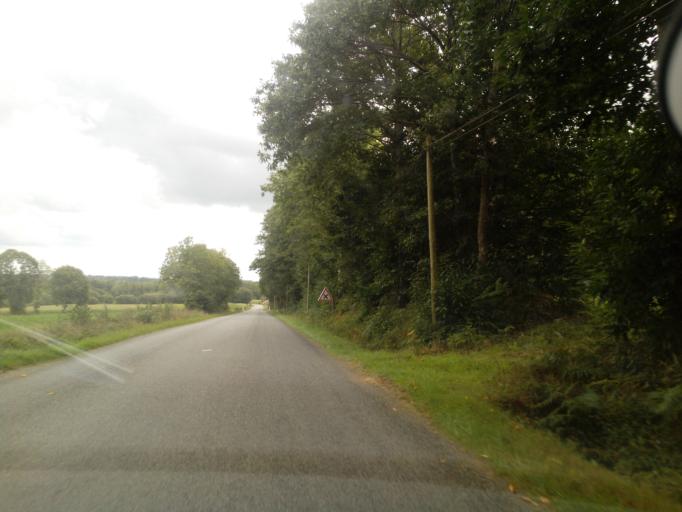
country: FR
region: Brittany
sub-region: Departement du Morbihan
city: Mauron
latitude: 48.0979
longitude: -2.3541
